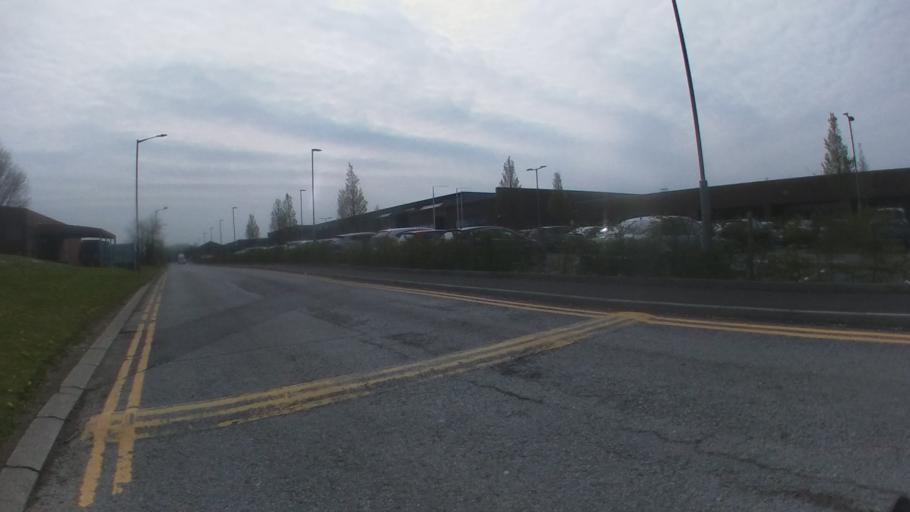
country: IE
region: Leinster
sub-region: Kilkenny
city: Kilkenny
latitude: 52.6468
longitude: -7.2146
